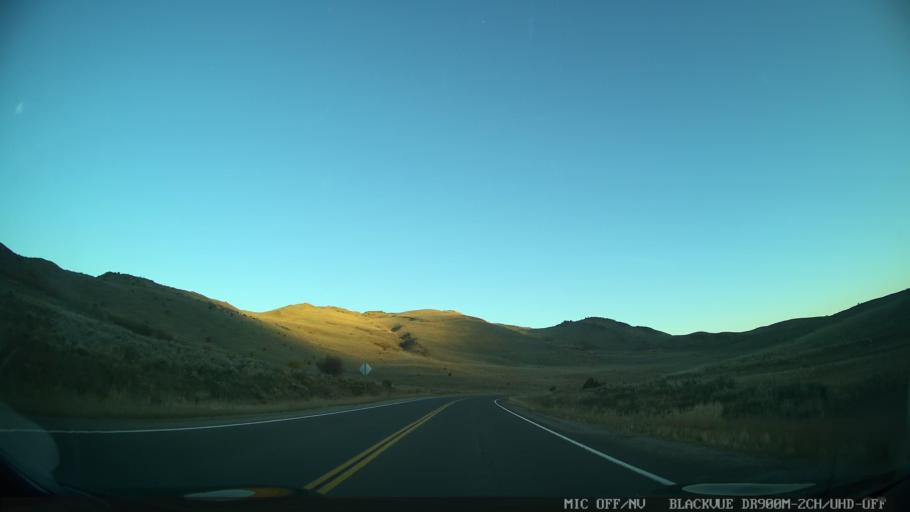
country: US
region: Colorado
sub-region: Eagle County
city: Edwards
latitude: 39.8110
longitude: -106.6742
